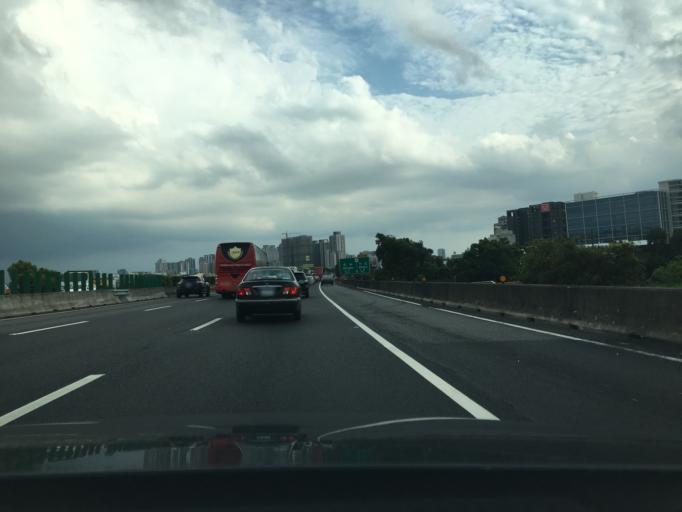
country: TW
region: Taiwan
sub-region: Hsinchu
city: Zhubei
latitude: 24.8445
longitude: 121.0215
